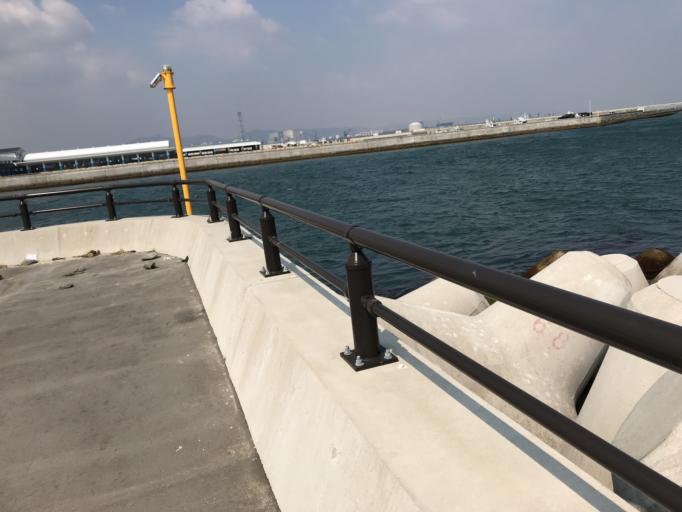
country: JP
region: Miyagi
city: Marumori
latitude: 37.8280
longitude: 140.9770
